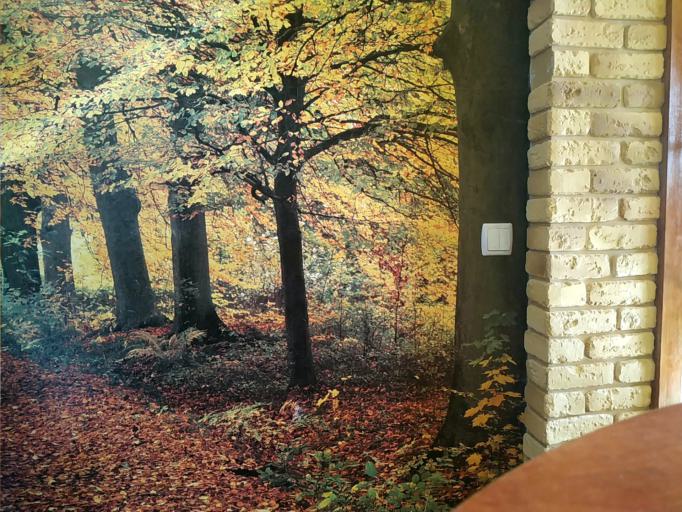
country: RU
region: Jaroslavl
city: Kukoboy
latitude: 58.8117
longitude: 39.7722
